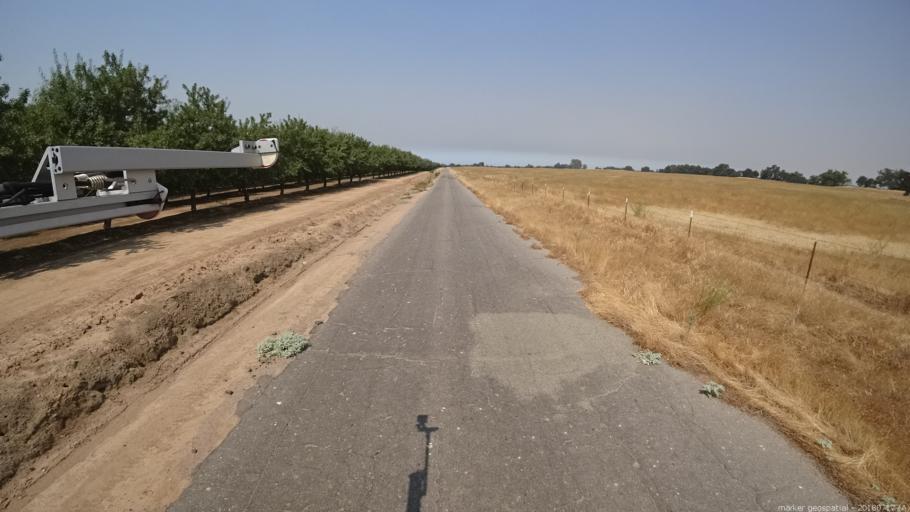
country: US
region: California
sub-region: Madera County
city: Fairmead
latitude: 37.1415
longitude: -120.1501
